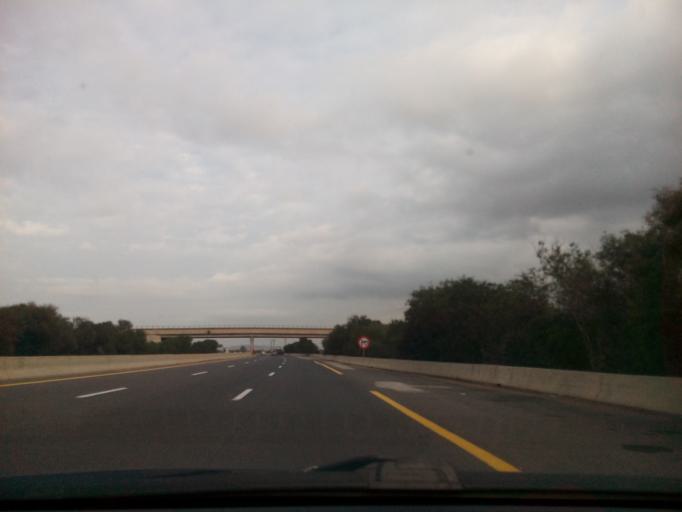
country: DZ
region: Mascara
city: Mascara
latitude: 35.6235
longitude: 0.0733
